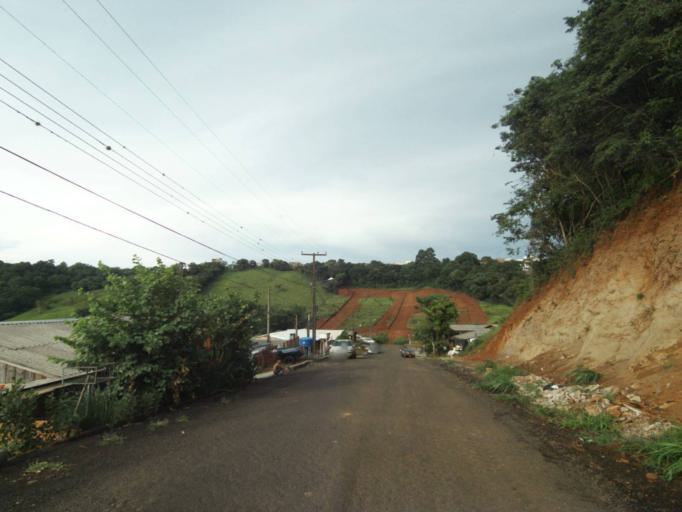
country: BR
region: Parana
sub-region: Guaraniacu
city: Guaraniacu
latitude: -25.1019
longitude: -52.8758
